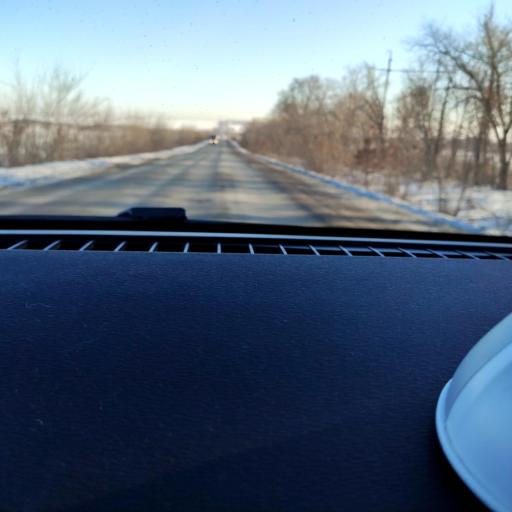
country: RU
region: Samara
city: Spiridonovka
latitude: 53.1446
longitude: 50.5346
